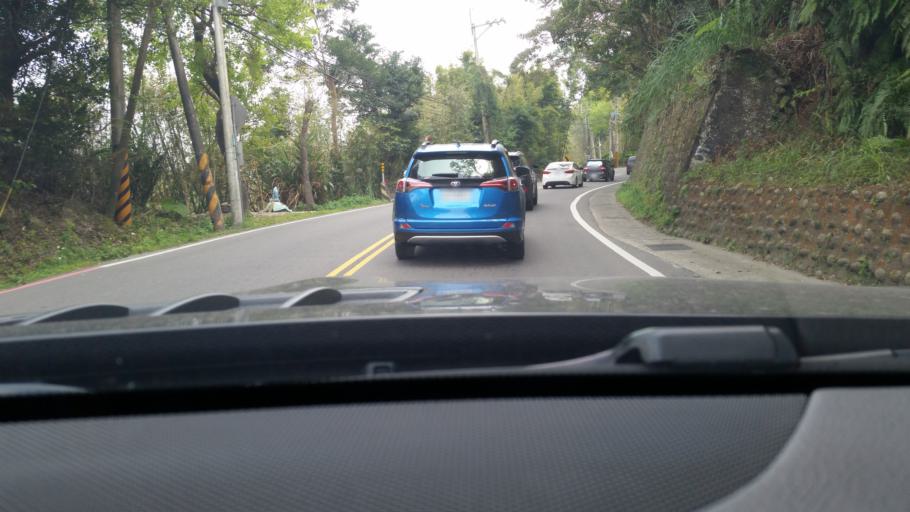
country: TW
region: Taiwan
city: Daxi
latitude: 24.8325
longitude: 121.3243
